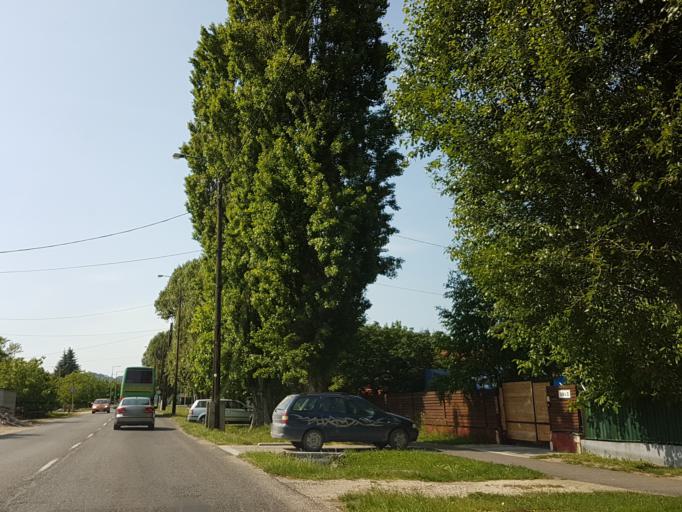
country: HU
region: Veszprem
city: Balatonalmadi
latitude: 47.0350
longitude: 18.0235
